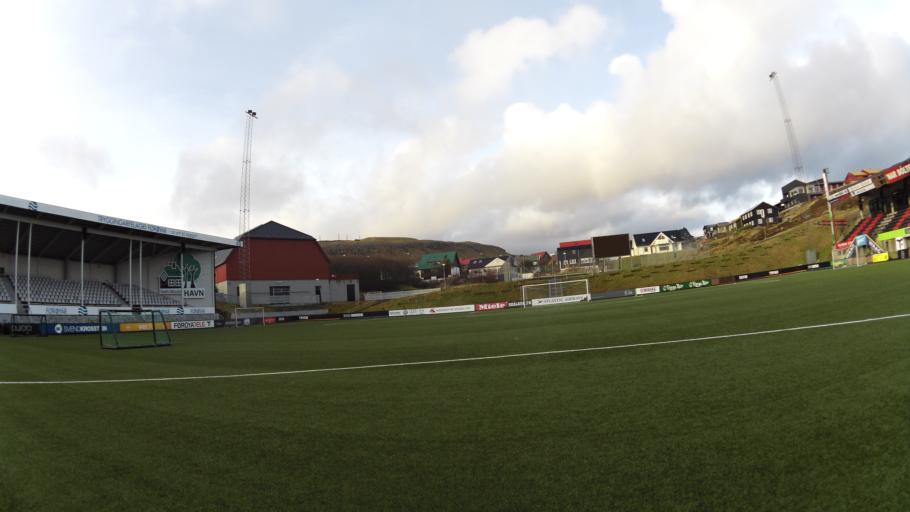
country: FO
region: Streymoy
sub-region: Torshavn
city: Torshavn
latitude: 62.0192
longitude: -6.7810
